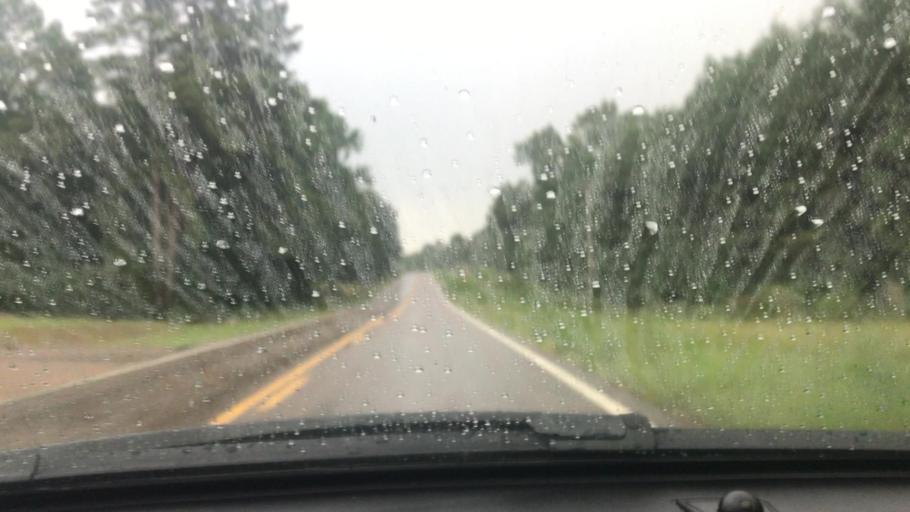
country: US
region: Mississippi
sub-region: Pike County
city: Summit
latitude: 31.3072
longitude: -90.5177
